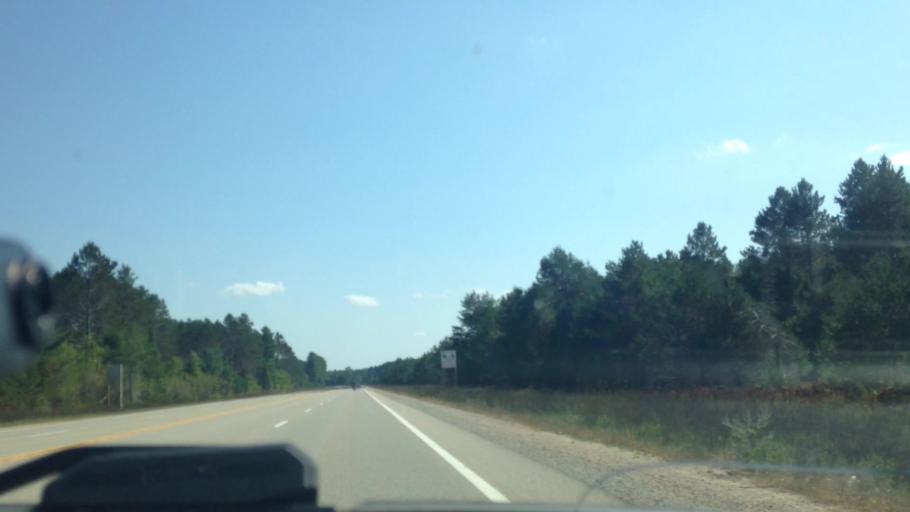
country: US
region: Michigan
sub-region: Alger County
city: Munising
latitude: 46.3545
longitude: -86.5089
